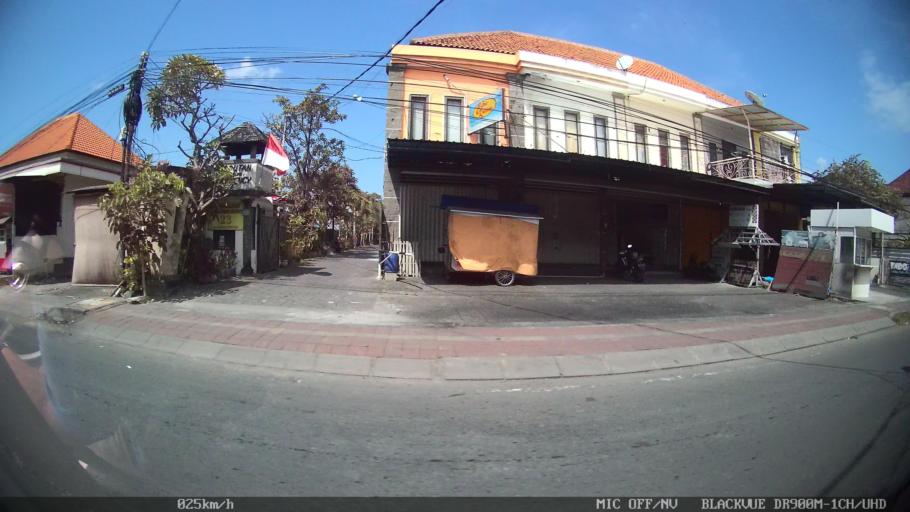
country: ID
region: Bali
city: Karyadharma
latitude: -8.6868
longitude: 115.1860
